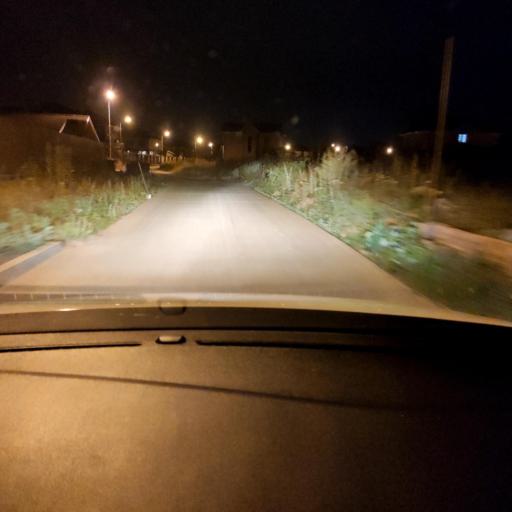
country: RU
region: Tatarstan
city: Osinovo
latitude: 55.8603
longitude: 48.7905
